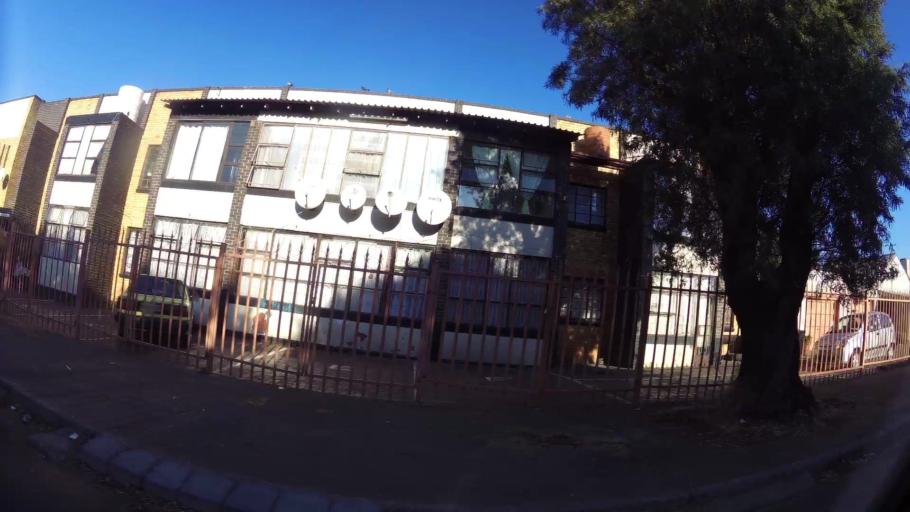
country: ZA
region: Gauteng
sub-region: Ekurhuleni Metropolitan Municipality
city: Germiston
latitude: -26.1963
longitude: 28.1475
